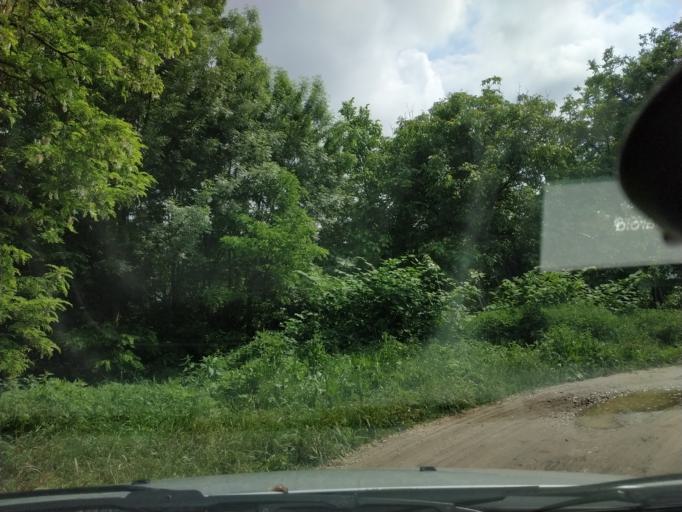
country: RS
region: Central Serbia
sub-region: Nisavski Okrug
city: Aleksinac
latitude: 43.4267
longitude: 21.5857
